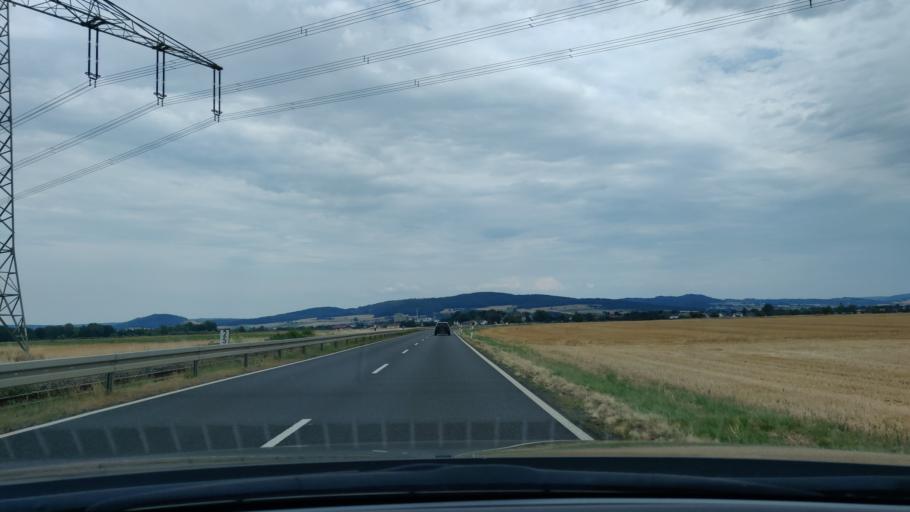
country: DE
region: Hesse
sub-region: Regierungsbezirk Kassel
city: Wabern
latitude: 51.1095
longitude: 9.3256
